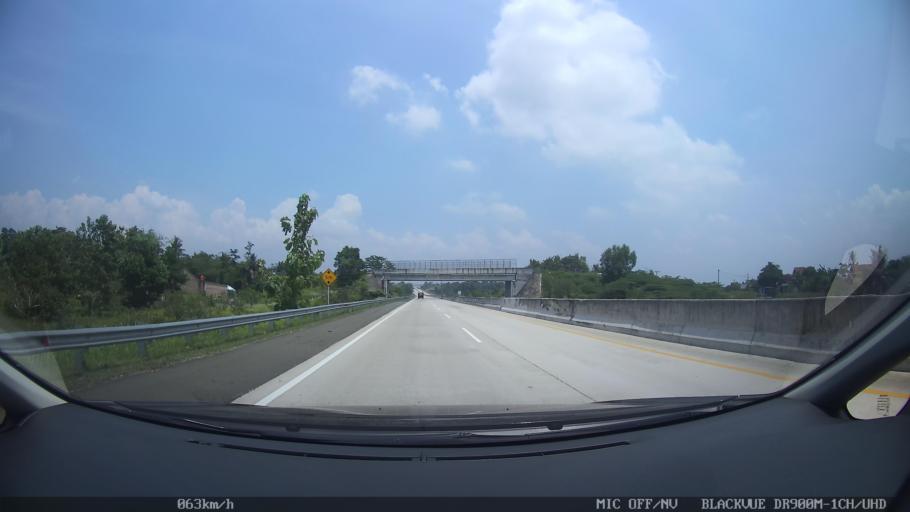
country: ID
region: Lampung
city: Kedaton
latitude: -5.3361
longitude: 105.3015
